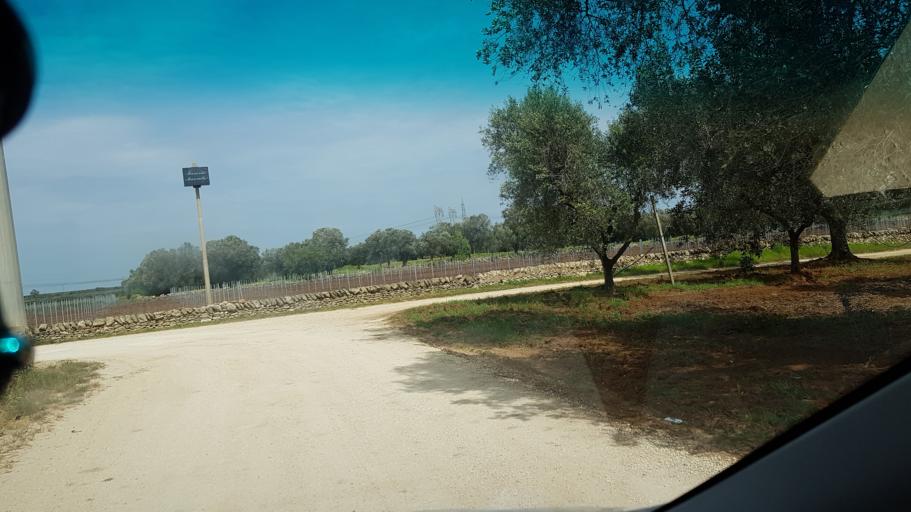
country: IT
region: Apulia
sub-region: Provincia di Brindisi
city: Mesagne
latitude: 40.6018
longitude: 17.8533
